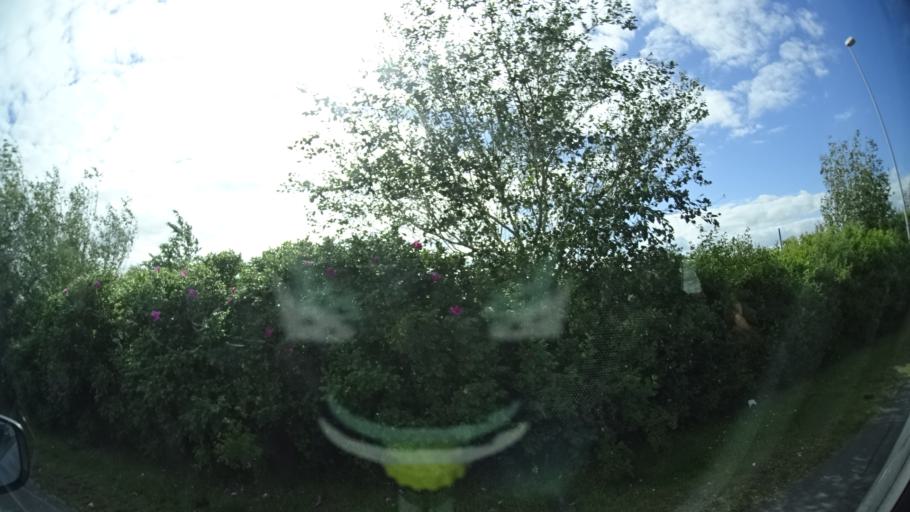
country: DK
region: Central Jutland
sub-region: Norddjurs Kommune
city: Grenaa
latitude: 56.5308
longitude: 10.7111
